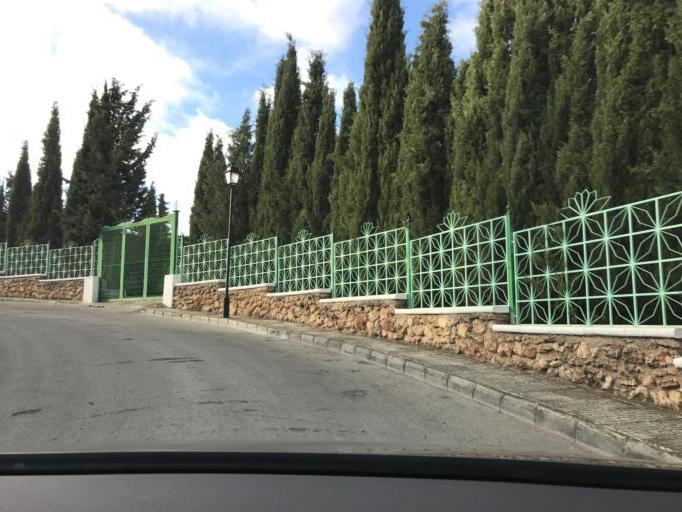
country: ES
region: Andalusia
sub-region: Provincia de Granada
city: Monachil
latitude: 37.1195
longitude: -3.5468
